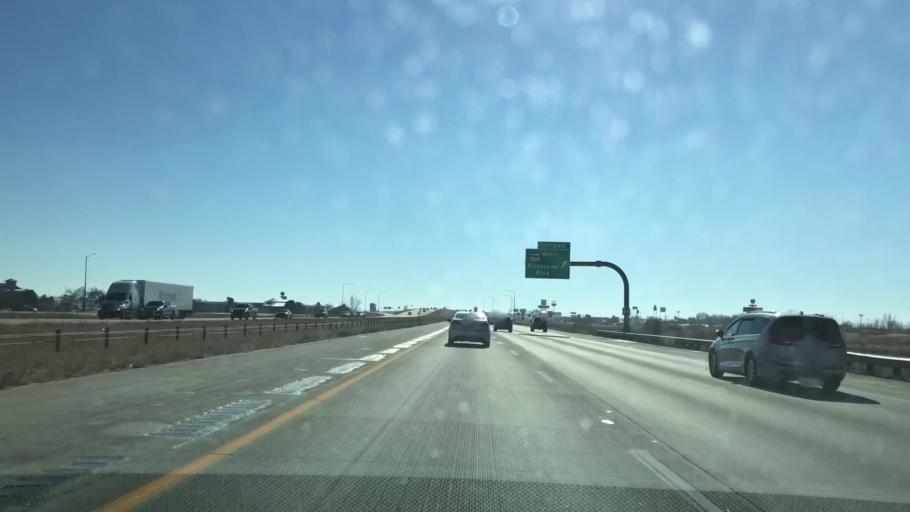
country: US
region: Colorado
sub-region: Weld County
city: Mead
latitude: 40.1678
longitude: -104.9799
